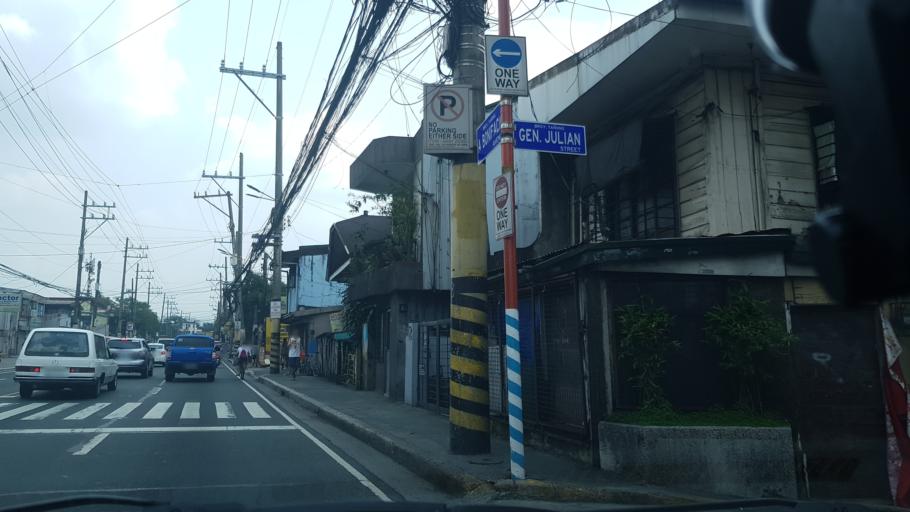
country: PH
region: Metro Manila
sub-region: Marikina
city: Calumpang
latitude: 14.6348
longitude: 121.0878
